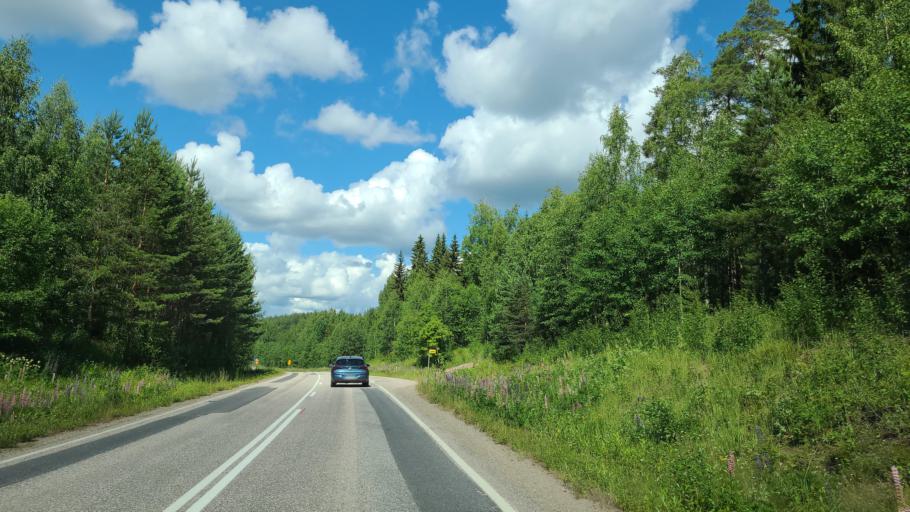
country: FI
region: Northern Savo
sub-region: Koillis-Savo
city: Kaavi
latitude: 62.9196
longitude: 28.6997
